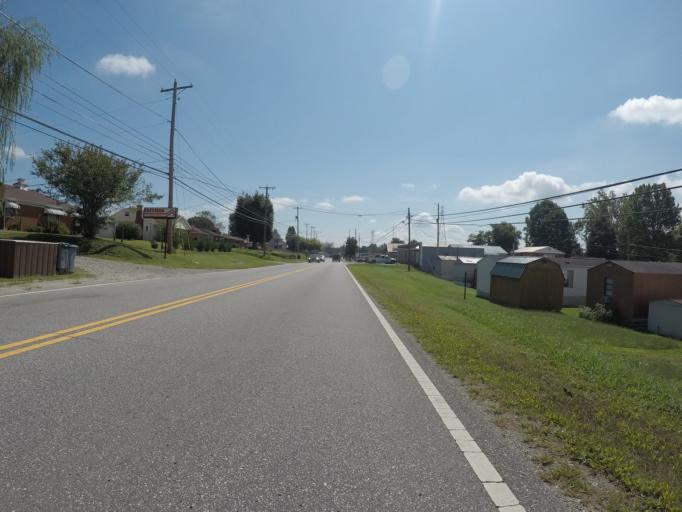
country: US
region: Ohio
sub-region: Lawrence County
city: South Point
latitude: 38.4163
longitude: -82.5845
